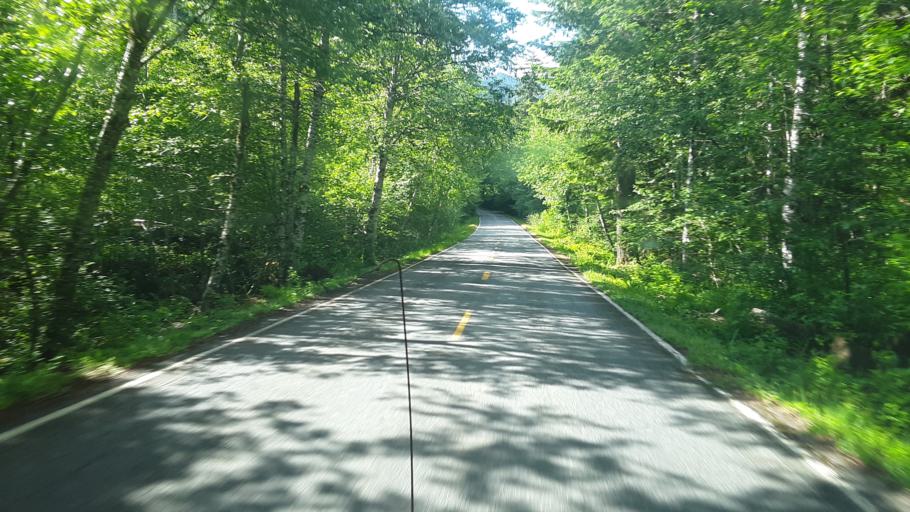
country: US
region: Washington
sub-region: Pierce County
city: Buckley
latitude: 46.7753
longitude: -121.5506
